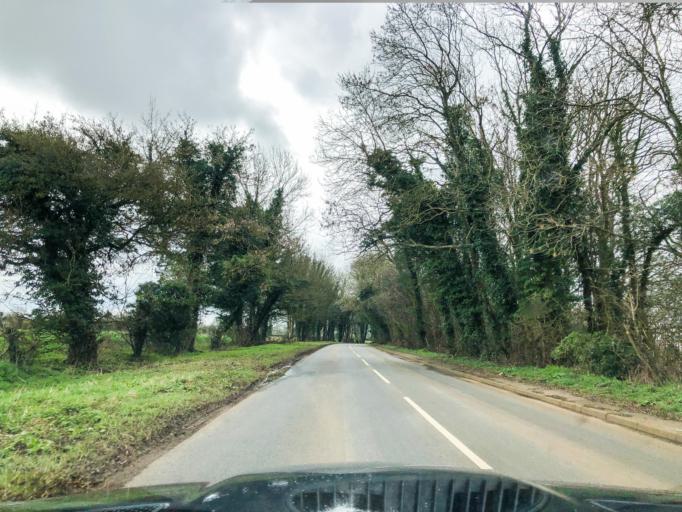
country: GB
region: England
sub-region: Oxfordshire
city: Hanwell
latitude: 52.1296
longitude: -1.4459
